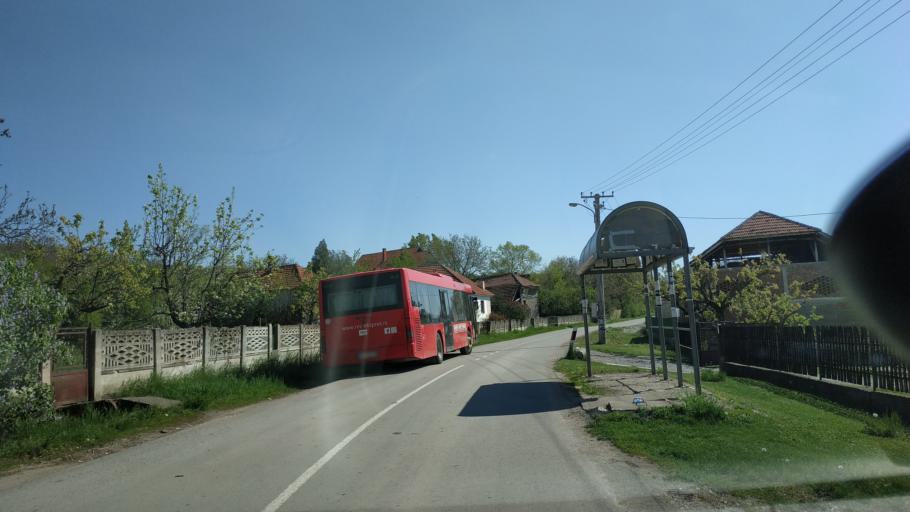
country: RS
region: Central Serbia
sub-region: Nisavski Okrug
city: Nis
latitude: 43.4642
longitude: 21.8619
